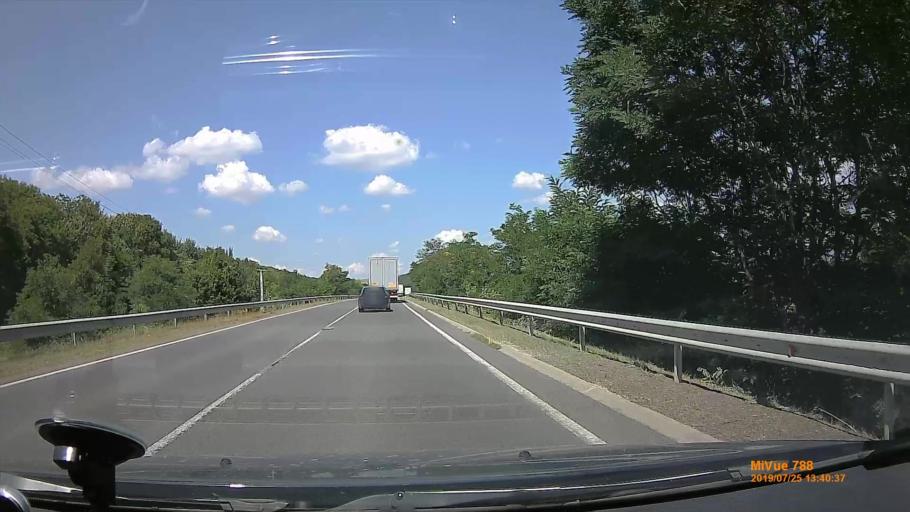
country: HU
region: Borsod-Abauj-Zemplen
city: Gonc
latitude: 48.4390
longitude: 21.1842
